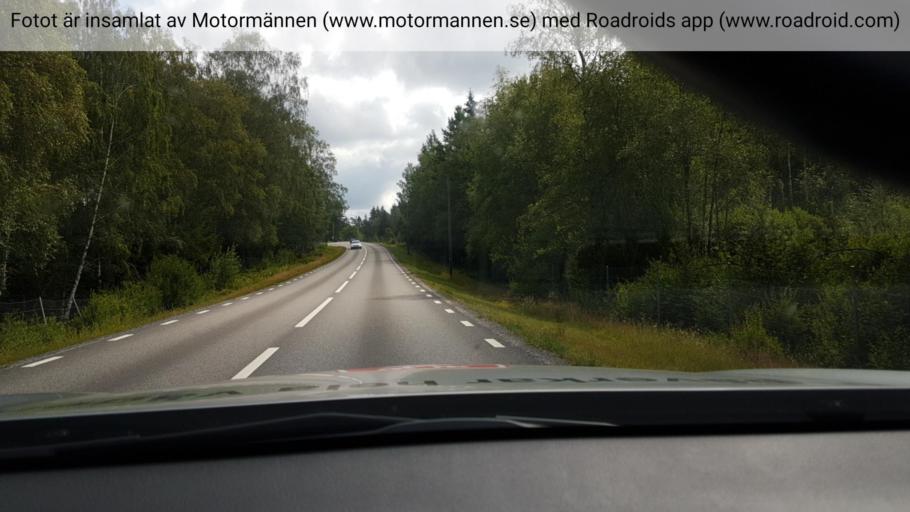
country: SE
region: Vaestra Goetaland
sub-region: Marks Kommun
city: Fritsla
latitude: 57.4817
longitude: 12.8124
